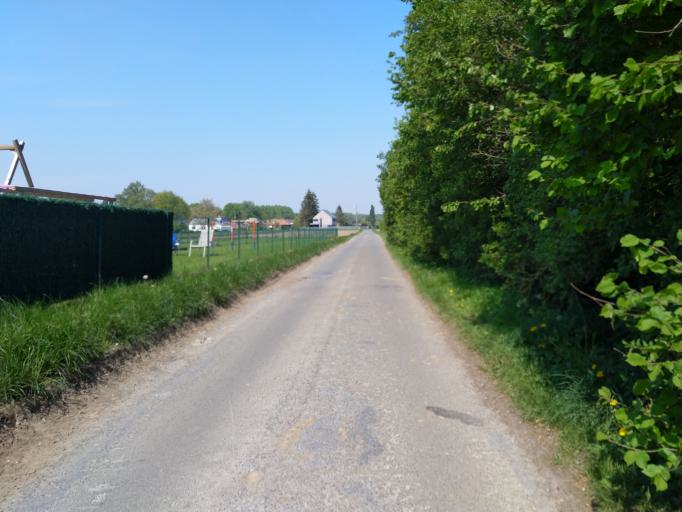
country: BE
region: Wallonia
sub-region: Province du Hainaut
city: Mons
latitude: 50.4358
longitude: 4.0198
